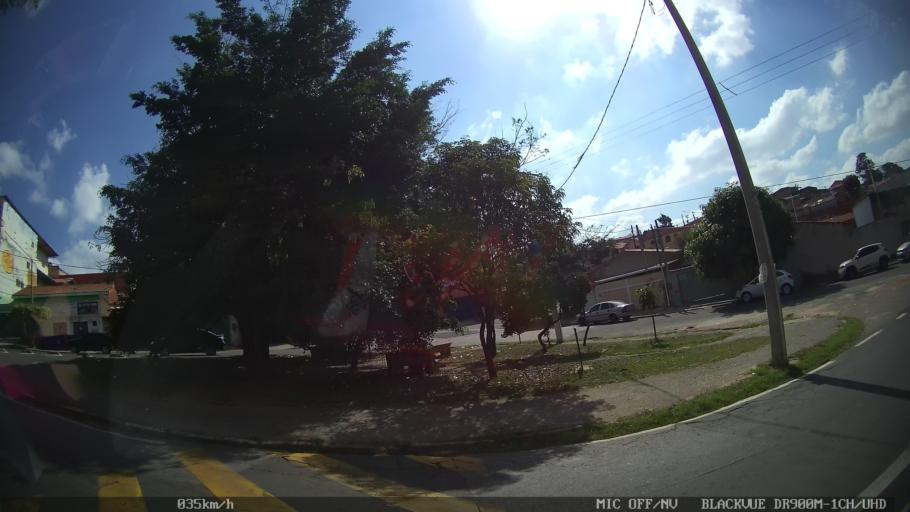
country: BR
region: Sao Paulo
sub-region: Campinas
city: Campinas
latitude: -22.9402
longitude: -47.1136
